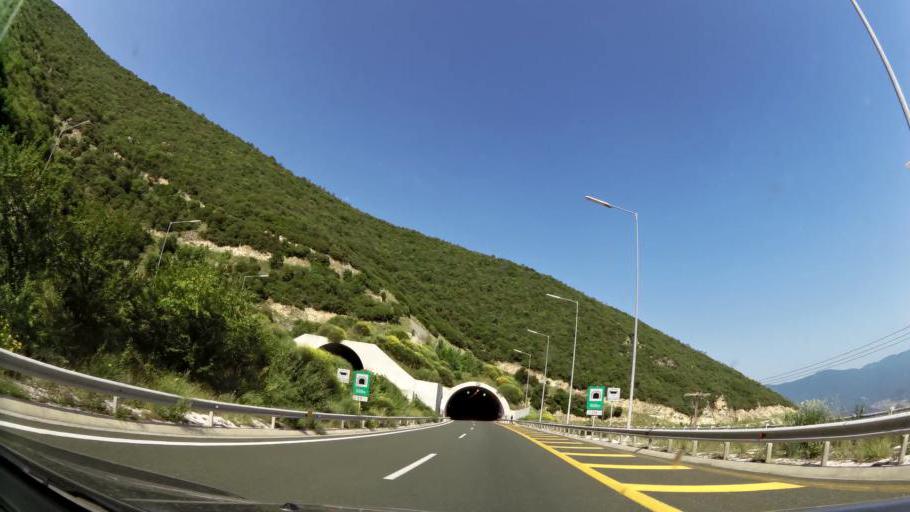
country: GR
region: Central Macedonia
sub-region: Nomos Imathias
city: Rizomata
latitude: 40.3804
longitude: 22.1041
